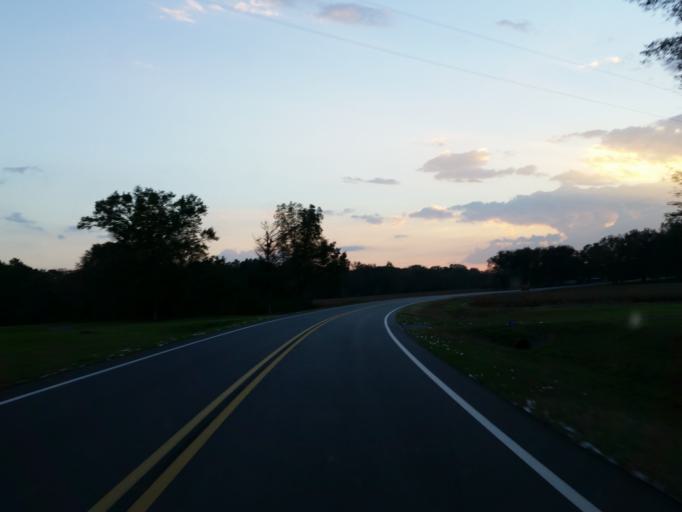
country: US
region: Georgia
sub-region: Pulaski County
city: Hawkinsville
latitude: 32.2109
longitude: -83.5309
